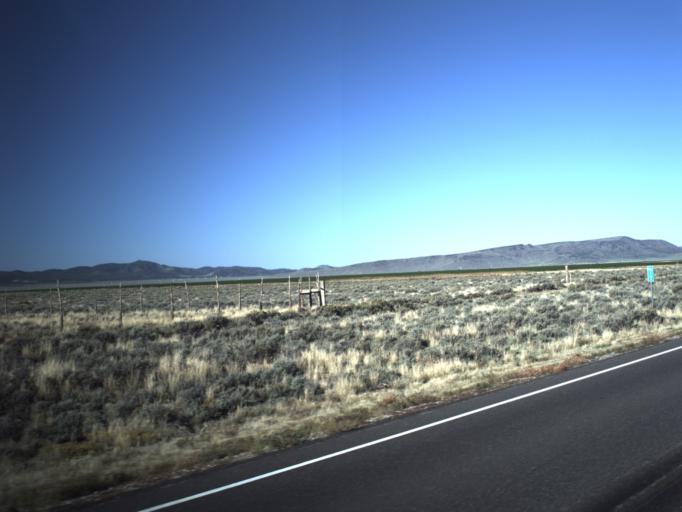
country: US
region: Utah
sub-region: Washington County
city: Enterprise
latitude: 37.7573
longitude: -113.7909
